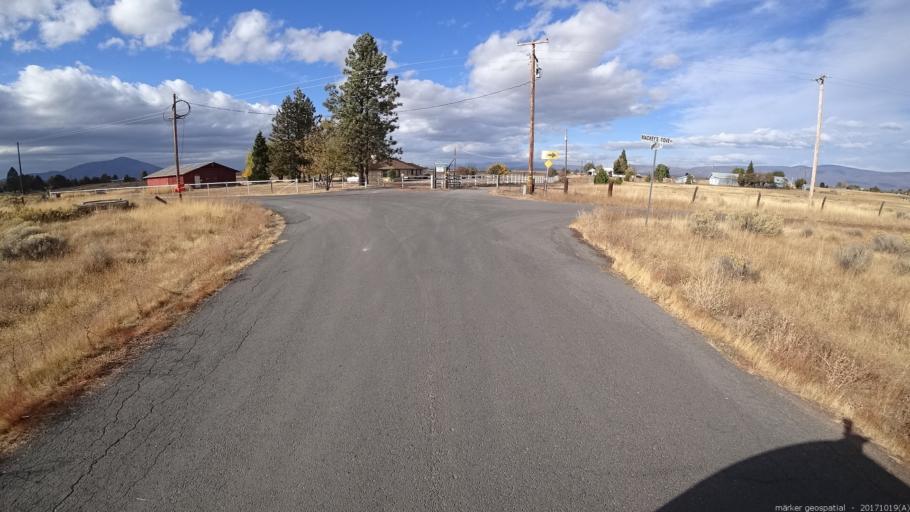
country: US
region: California
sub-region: Shasta County
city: Burney
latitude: 41.0215
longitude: -121.4369
